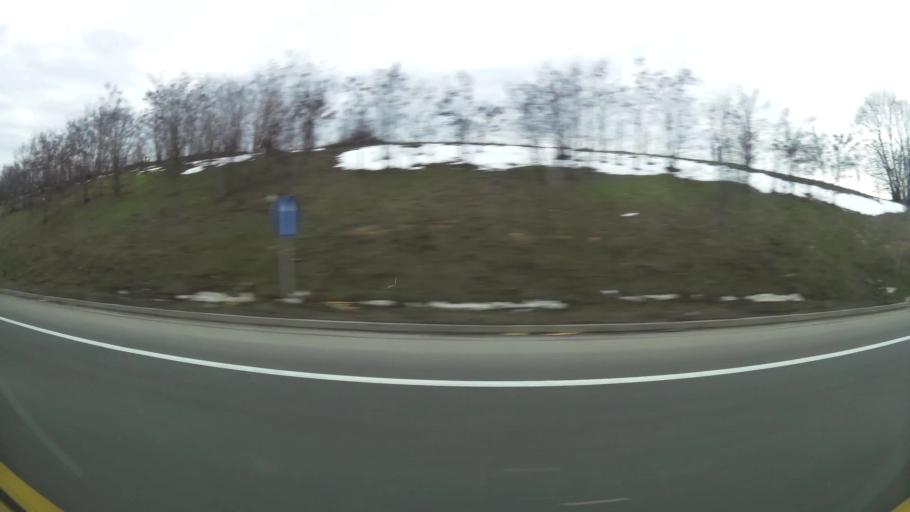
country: RS
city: Ostruznica
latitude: 44.7226
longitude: 20.3584
